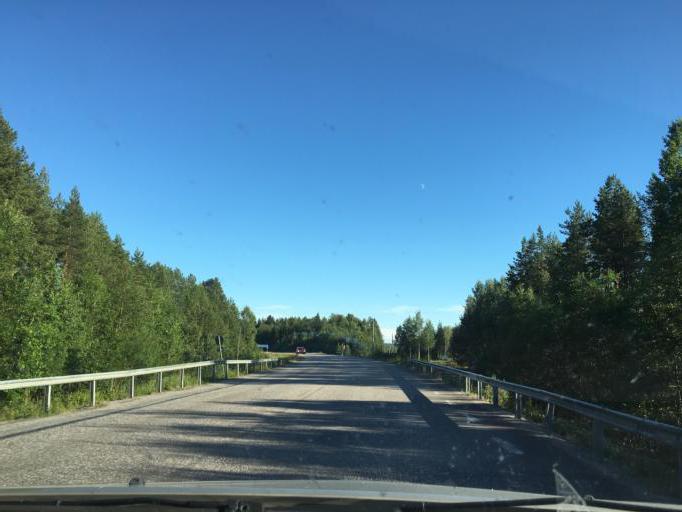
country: SE
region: Norrbotten
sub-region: Kalix Kommun
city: Rolfs
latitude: 65.9061
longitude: 22.9299
